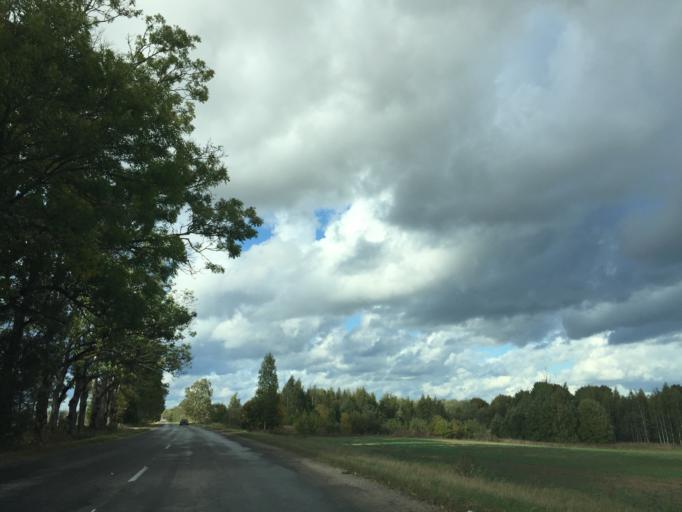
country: LV
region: Malpils
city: Malpils
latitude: 56.9807
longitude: 24.9117
